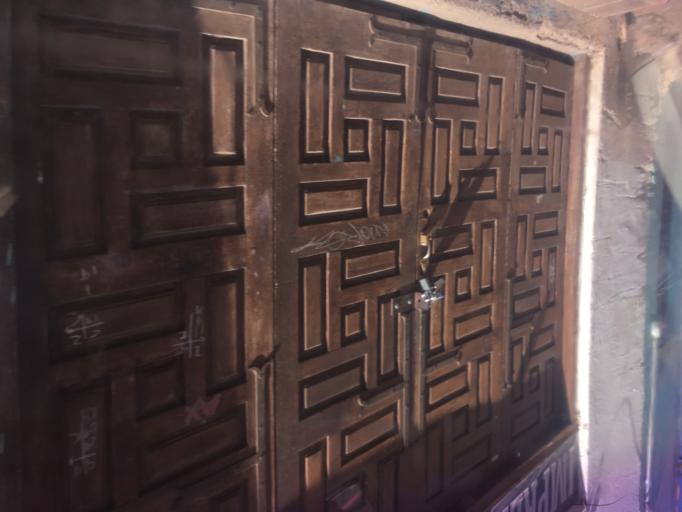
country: MX
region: Guanajuato
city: Guanajuato
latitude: 21.0172
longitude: -101.2514
